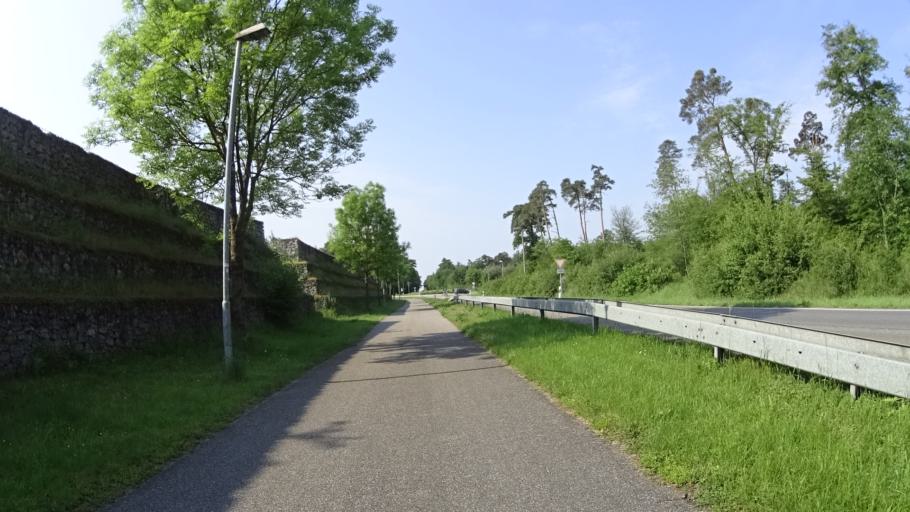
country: DE
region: Baden-Wuerttemberg
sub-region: Karlsruhe Region
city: Waghausel
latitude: 49.2345
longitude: 8.5345
